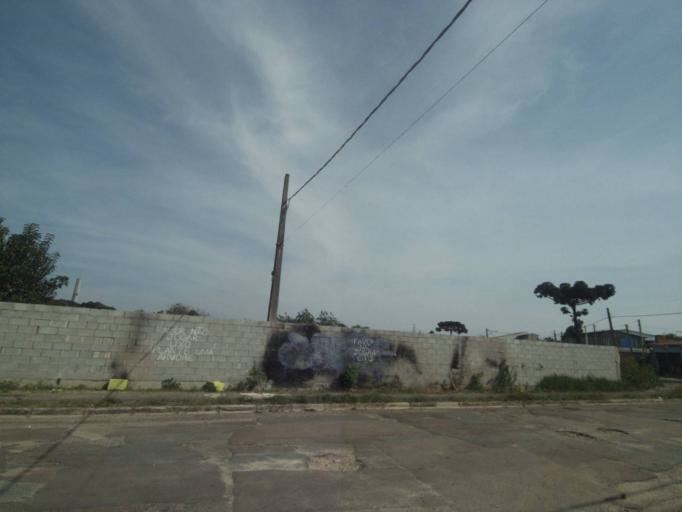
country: BR
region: Parana
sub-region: Curitiba
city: Curitiba
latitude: -25.4637
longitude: -49.3192
